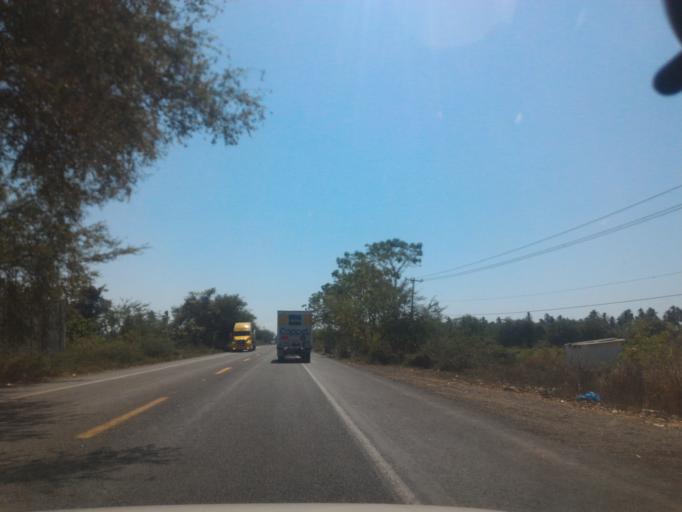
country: MX
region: Colima
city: Tecoman
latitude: 18.8437
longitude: -103.8245
